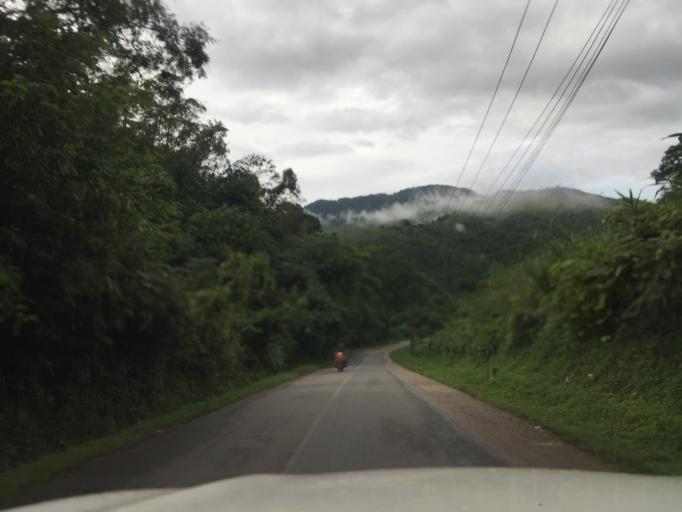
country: LA
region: Oudomxai
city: Muang La
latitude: 20.7962
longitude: 102.0854
